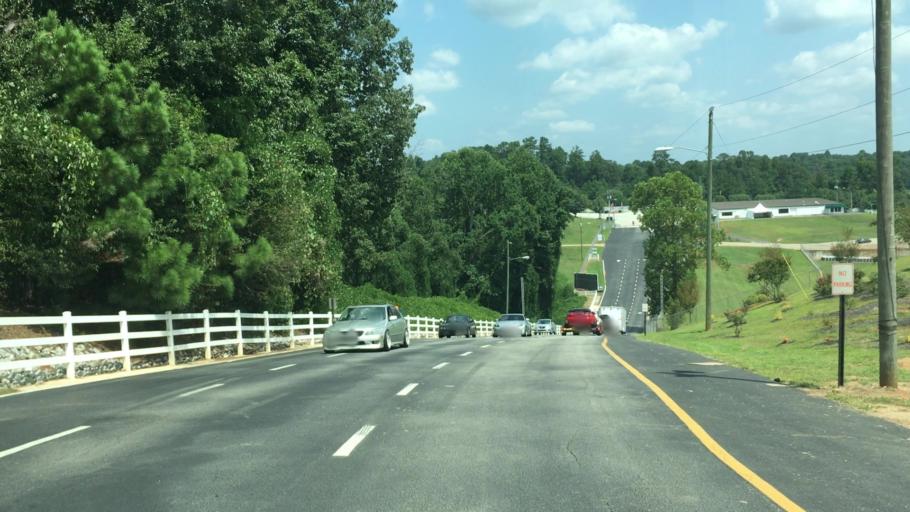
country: US
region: Georgia
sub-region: Jackson County
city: Braselton
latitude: 34.1504
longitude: -83.8181
